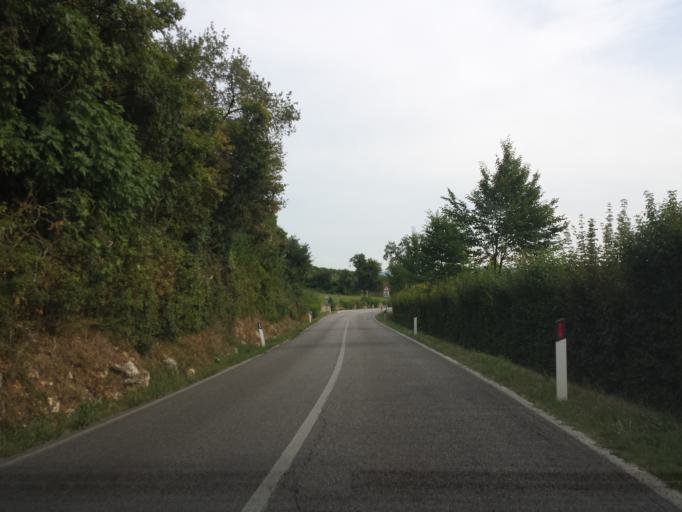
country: IT
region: Veneto
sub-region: Provincia di Vicenza
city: Sovizzo
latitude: 45.5374
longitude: 11.4376
